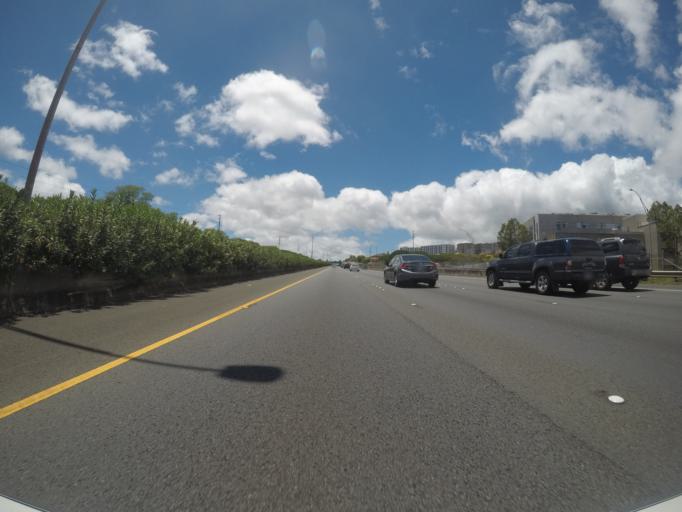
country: US
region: Hawaii
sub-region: Honolulu County
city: Halawa Heights
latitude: 21.3622
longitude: -157.9006
